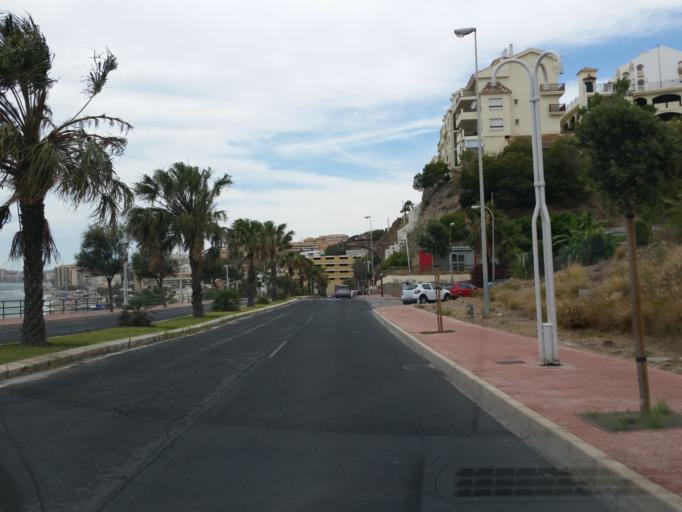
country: ES
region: Andalusia
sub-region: Provincia de Malaga
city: Benalmadena
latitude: 36.5739
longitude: -4.5859
